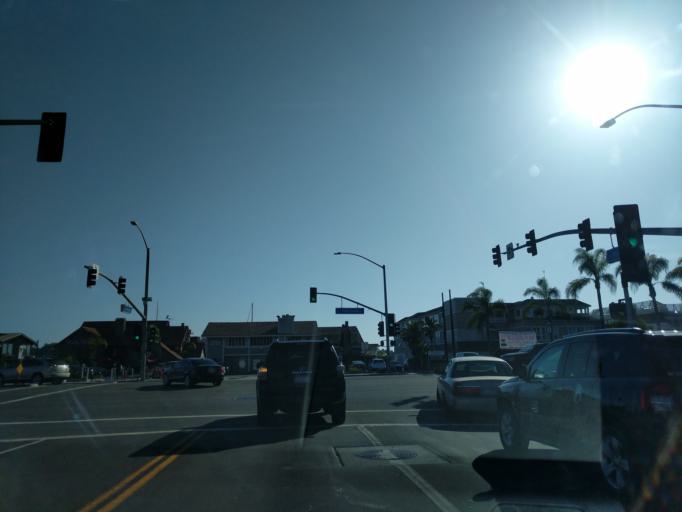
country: US
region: California
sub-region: Orange County
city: Newport Beach
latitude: 33.6207
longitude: -117.9242
